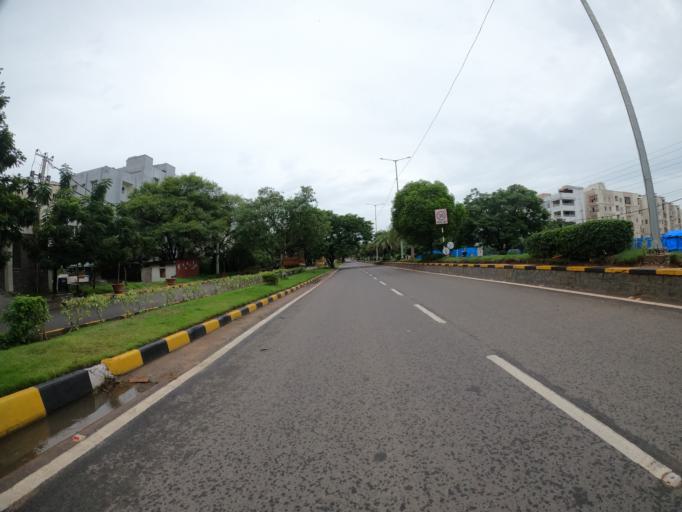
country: IN
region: Telangana
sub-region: Rangareddi
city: Kukatpalli
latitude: 17.4671
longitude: 78.3757
